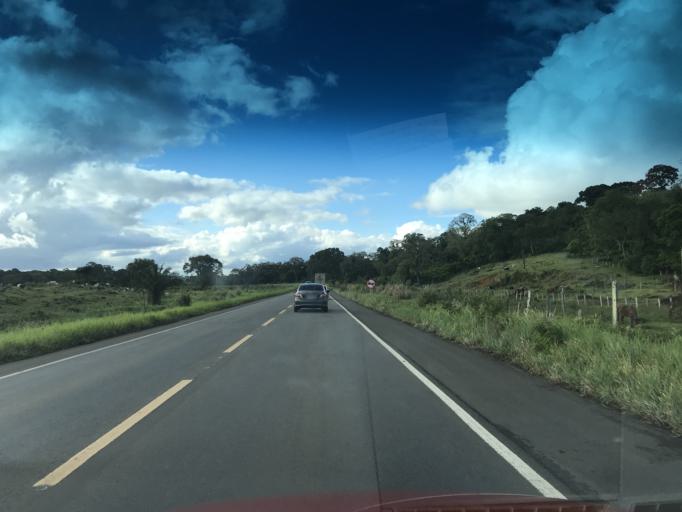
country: BR
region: Bahia
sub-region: Ibirapitanga
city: Ibirapitanga
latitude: -14.1589
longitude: -39.3276
